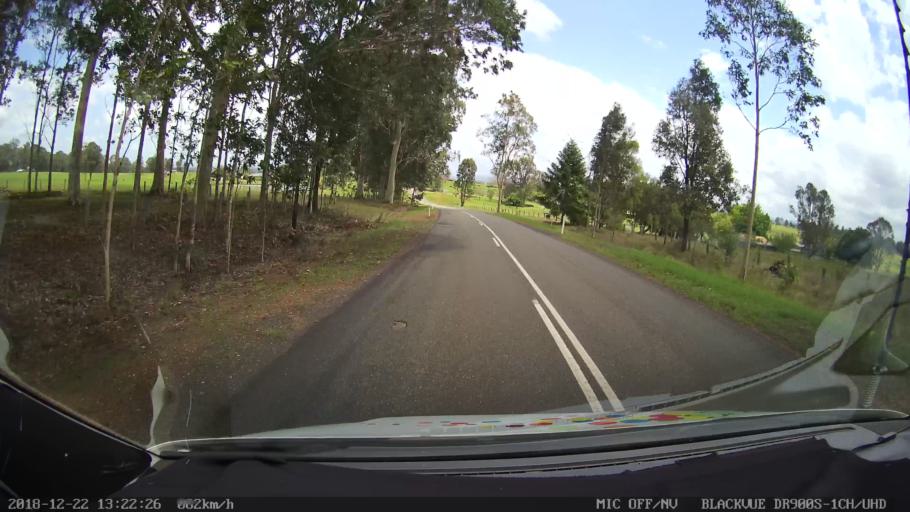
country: AU
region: New South Wales
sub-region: Clarence Valley
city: Coutts Crossing
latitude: -29.7866
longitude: 152.9117
